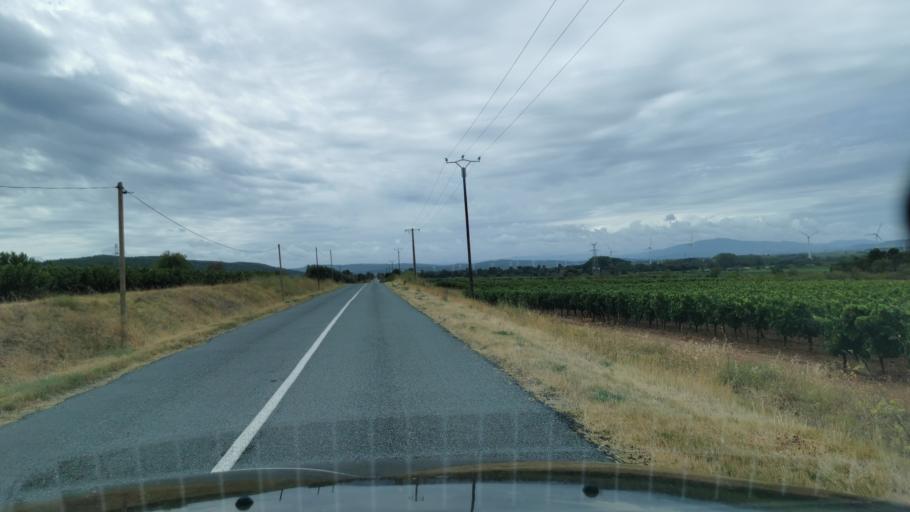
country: FR
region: Languedoc-Roussillon
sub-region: Departement de l'Aude
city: Nevian
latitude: 43.2045
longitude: 2.8712
